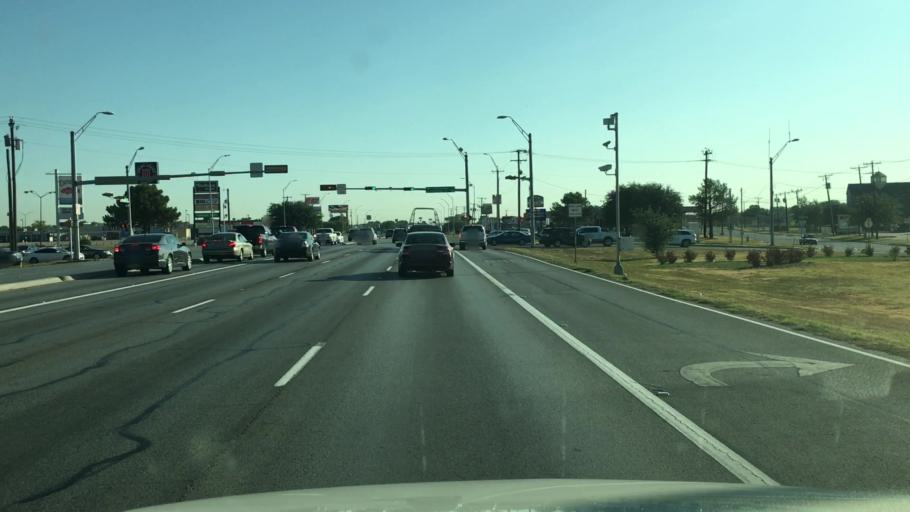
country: US
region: Texas
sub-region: Johnson County
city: Burleson
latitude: 32.5337
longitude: -97.3364
